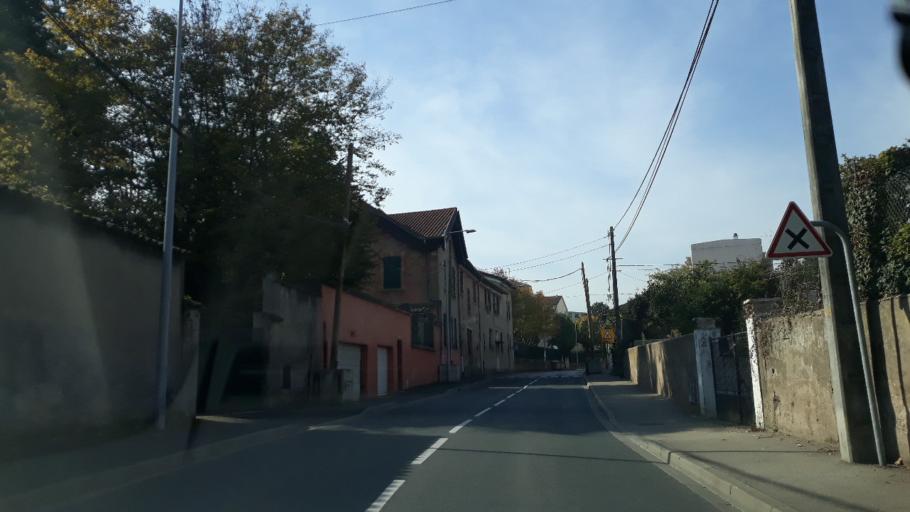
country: FR
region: Rhone-Alpes
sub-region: Departement du Rhone
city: Villefranche-sur-Saone
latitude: 45.9911
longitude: 4.7320
